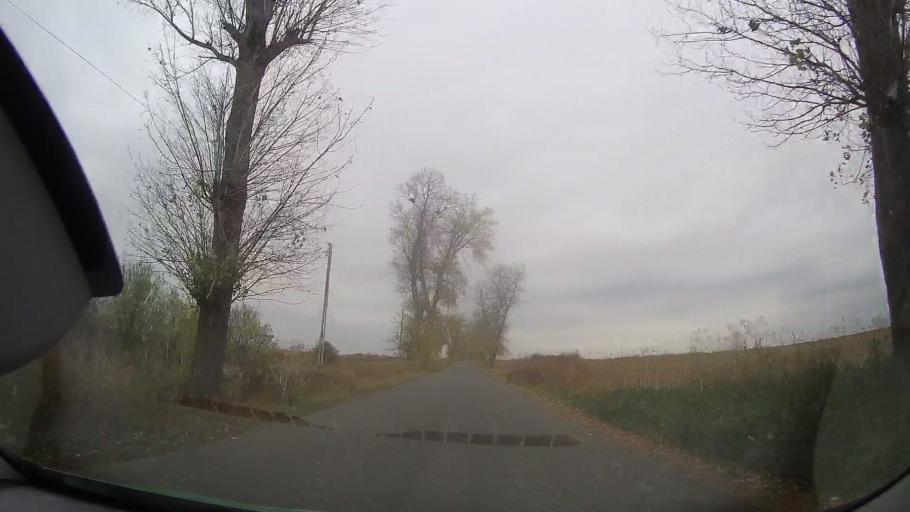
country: RO
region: Braila
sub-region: Comuna Ciocile
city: Ciocile
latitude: 44.8087
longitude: 27.2804
